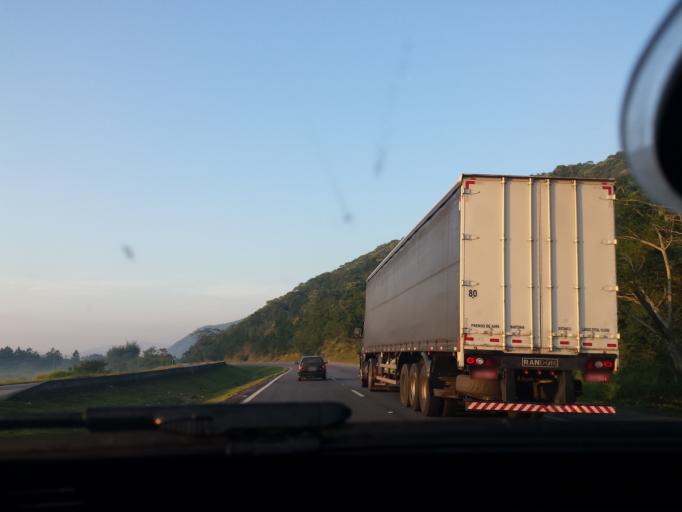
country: BR
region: Santa Catarina
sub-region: Florianopolis
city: Pantano do Sul
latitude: -27.8505
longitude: -48.6398
